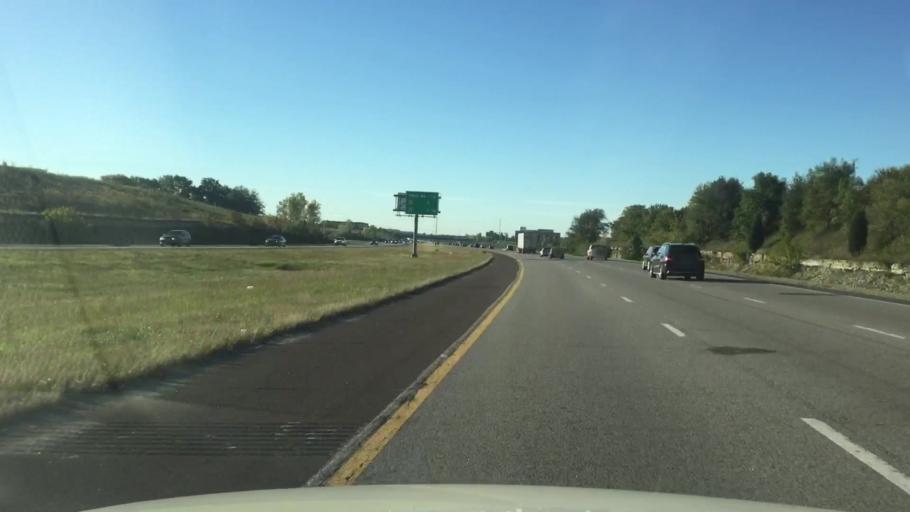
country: US
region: Kansas
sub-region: Johnson County
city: Lenexa
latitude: 38.9663
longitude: -94.7767
